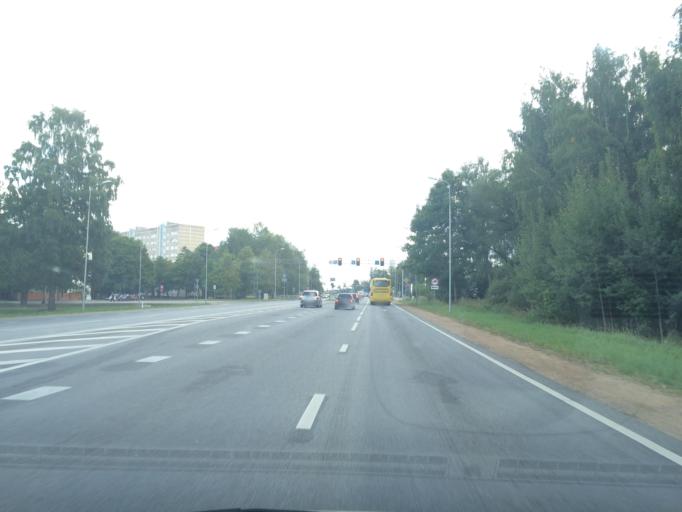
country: LV
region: Salaspils
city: Salaspils
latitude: 56.8532
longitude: 24.3299
